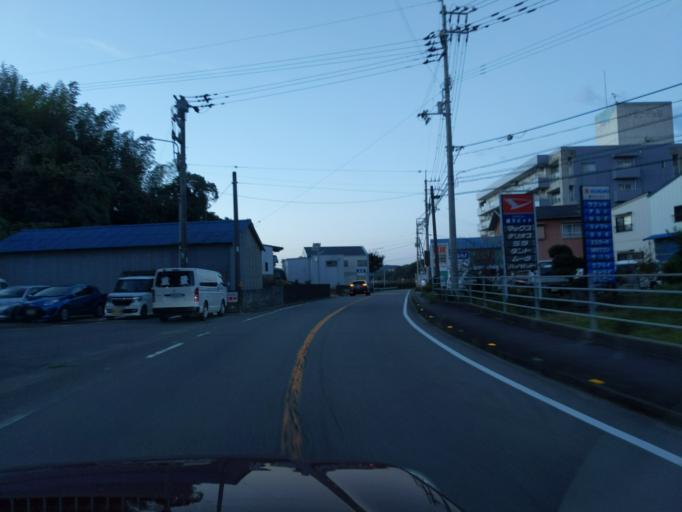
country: JP
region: Tokushima
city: Anan
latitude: 33.8641
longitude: 134.6319
